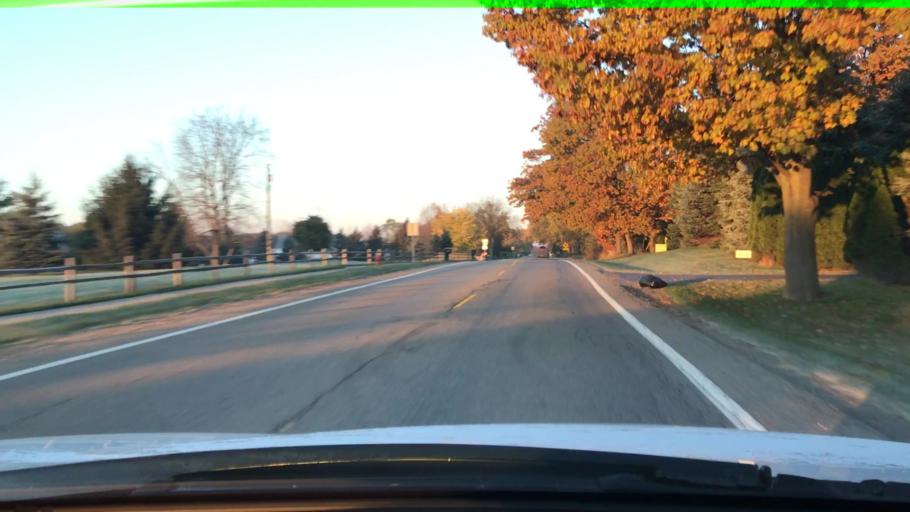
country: US
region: Michigan
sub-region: Oakland County
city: Clarkston
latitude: 42.7524
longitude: -83.3646
